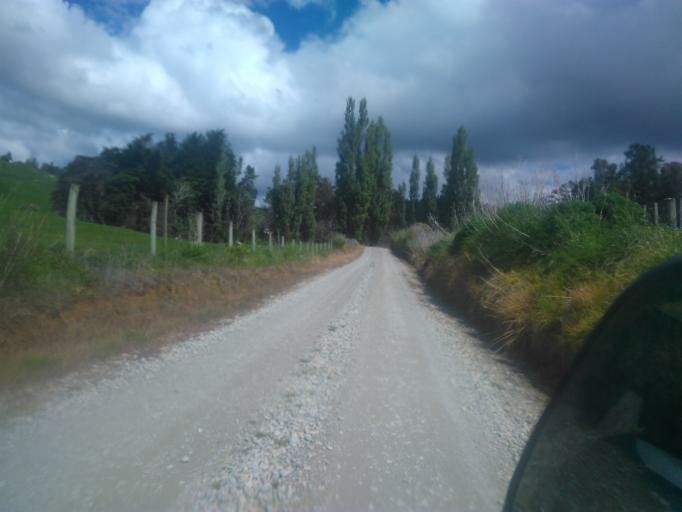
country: NZ
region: Hawke's Bay
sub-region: Wairoa District
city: Wairoa
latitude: -38.7597
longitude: 177.5956
